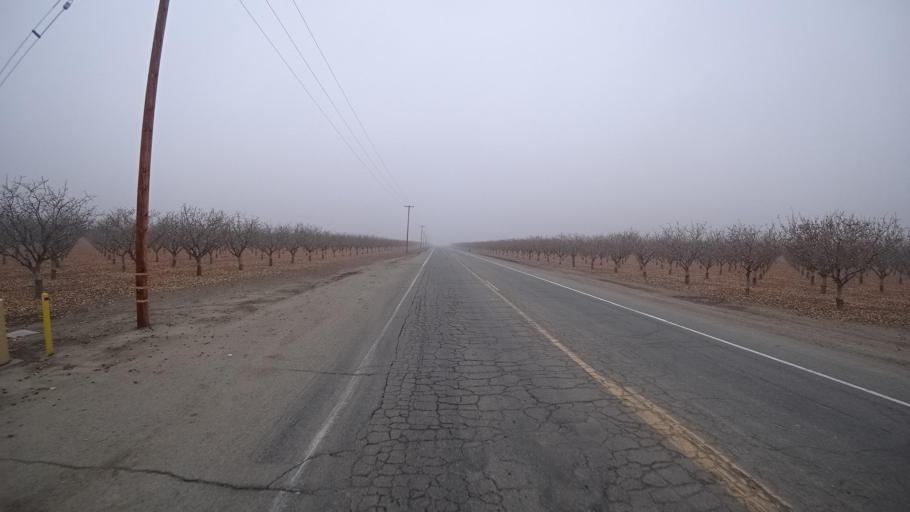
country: US
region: California
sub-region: Kern County
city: Buttonwillow
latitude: 35.3998
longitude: -119.5185
